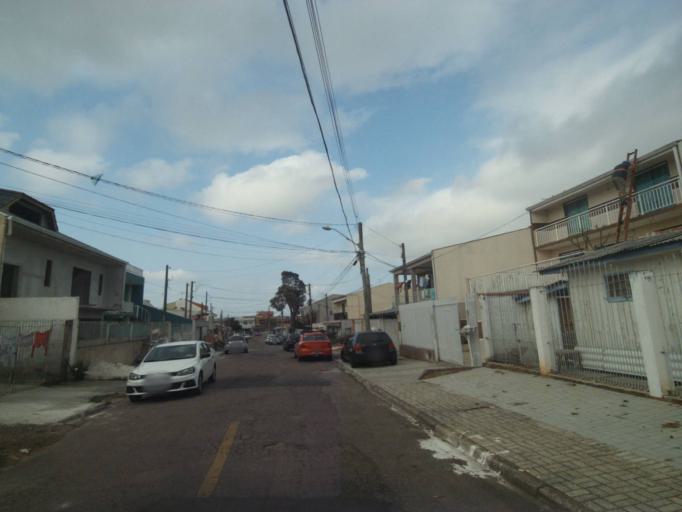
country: BR
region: Parana
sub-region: Sao Jose Dos Pinhais
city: Sao Jose dos Pinhais
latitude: -25.5472
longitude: -49.2598
